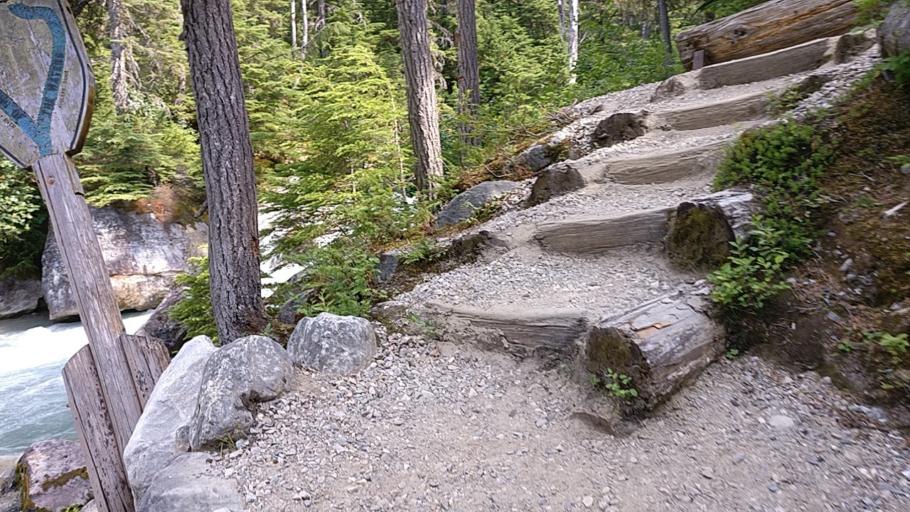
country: CA
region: British Columbia
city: Golden
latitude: 51.2597
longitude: -117.4900
